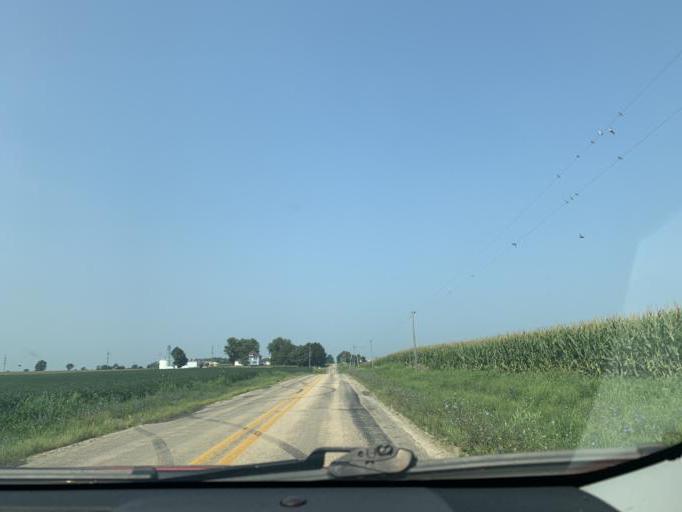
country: US
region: Illinois
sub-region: Carroll County
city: Milledgeville
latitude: 41.8480
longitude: -89.8150
